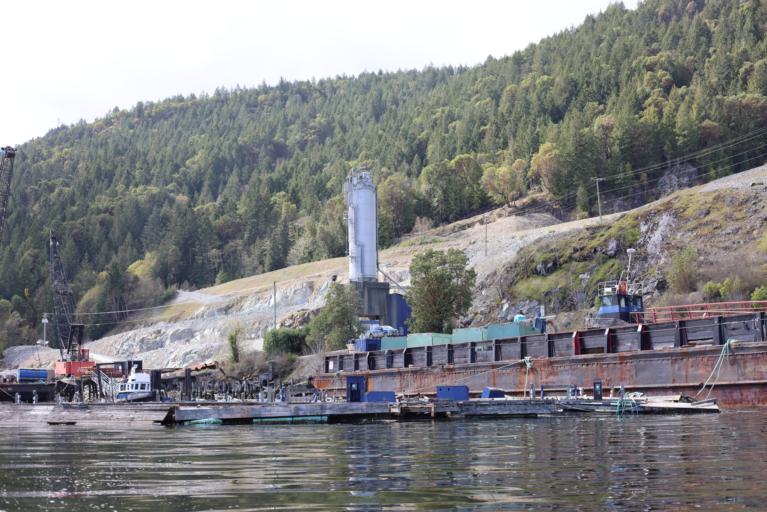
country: CA
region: British Columbia
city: North Saanich
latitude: 48.5876
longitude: -123.5203
